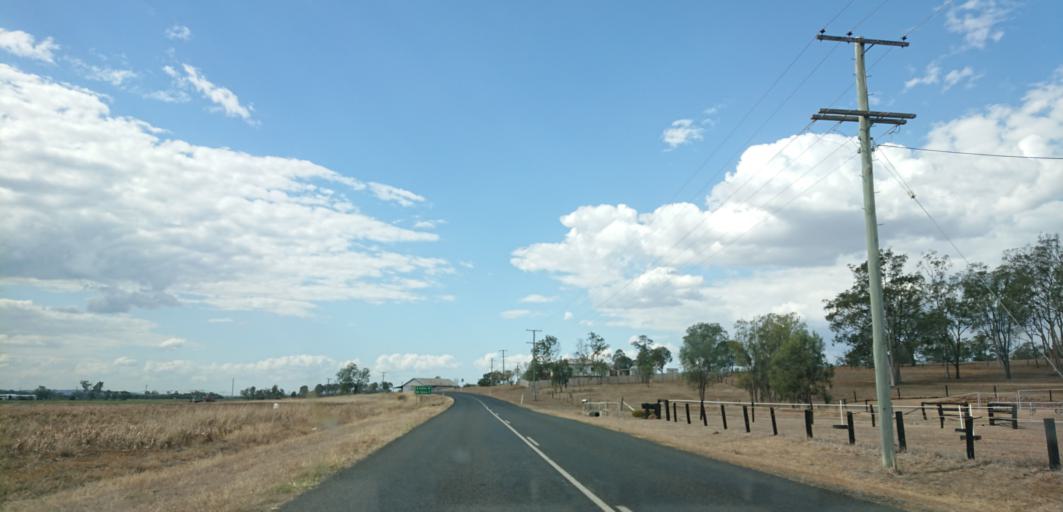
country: AU
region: Queensland
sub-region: Lockyer Valley
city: Gatton
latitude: -27.6210
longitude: 152.2050
